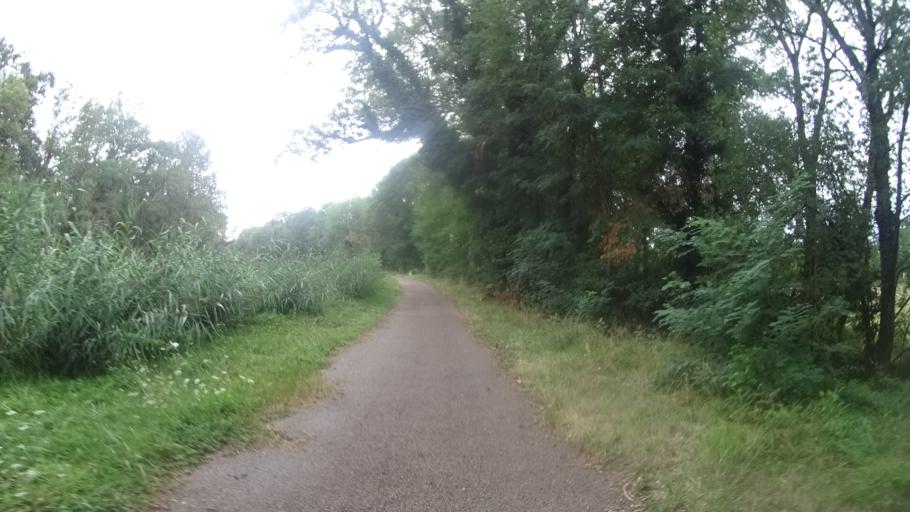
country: FR
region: Bourgogne
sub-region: Departement de la Nievre
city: Saint-Leger-des-Vignes
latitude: 46.8201
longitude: 3.4236
